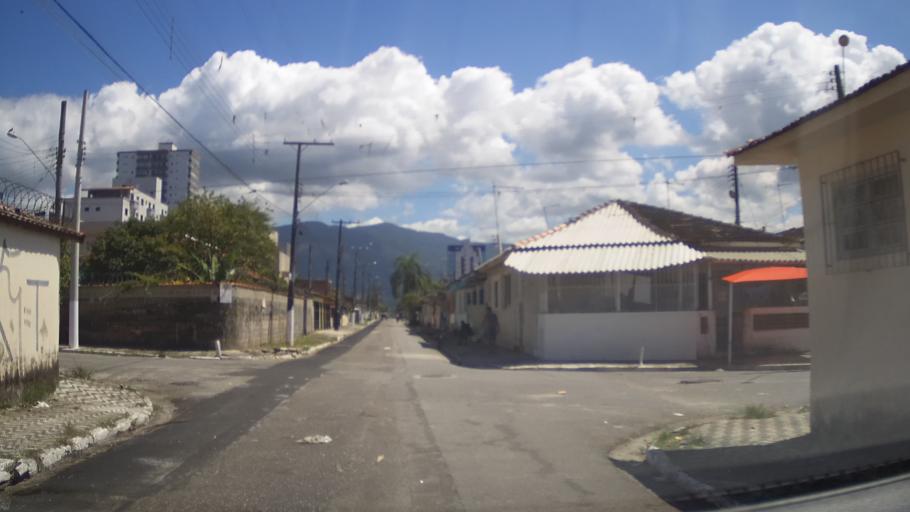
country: BR
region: Sao Paulo
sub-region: Mongagua
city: Mongagua
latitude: -24.0475
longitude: -46.5247
